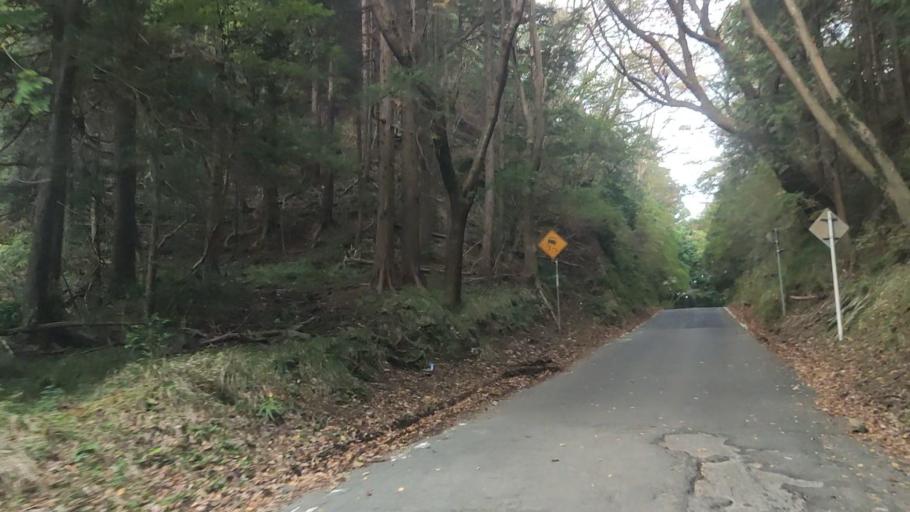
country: JP
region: Shizuoka
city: Ito
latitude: 34.9517
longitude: 139.0544
